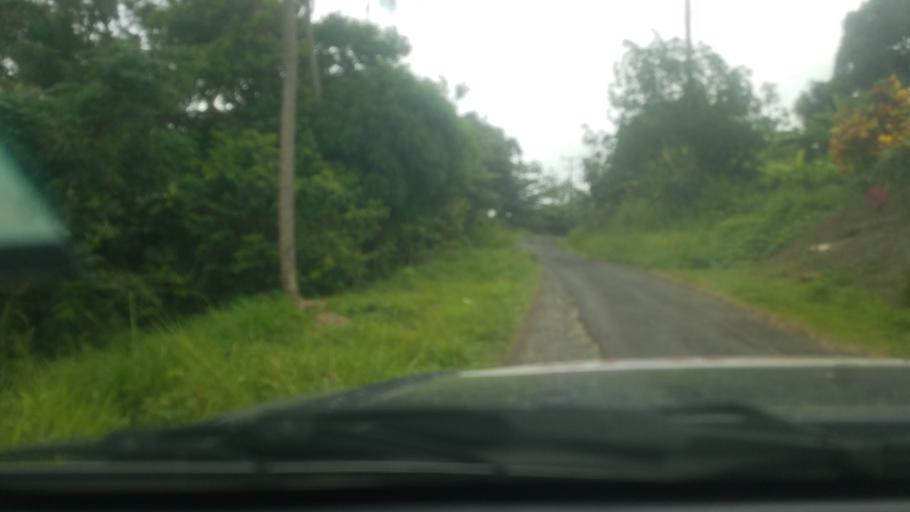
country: LC
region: Laborie Quarter
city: Laborie
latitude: 13.7757
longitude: -60.9798
